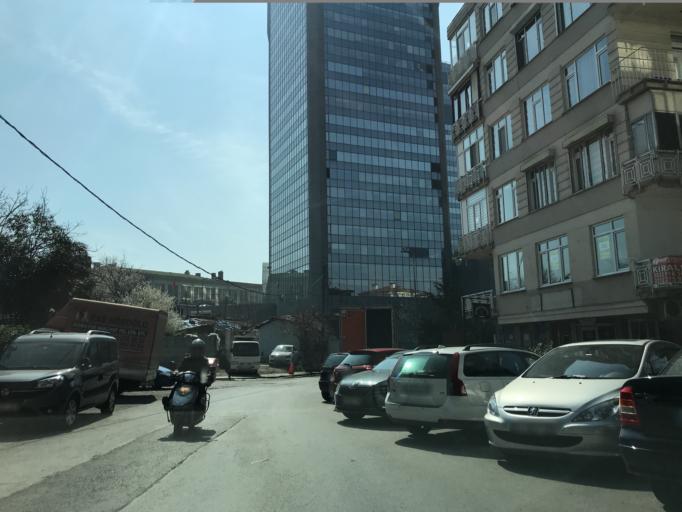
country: TR
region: Istanbul
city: Sisli
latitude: 41.0598
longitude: 29.0085
